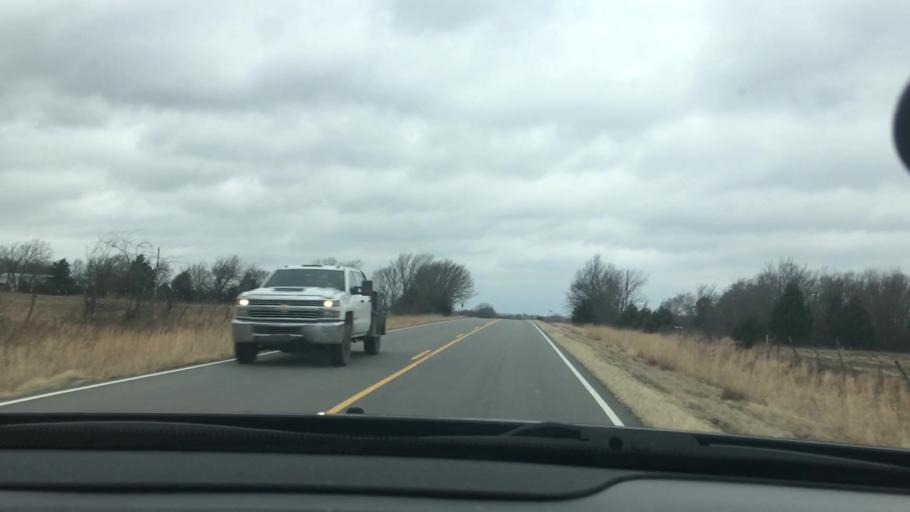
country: US
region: Oklahoma
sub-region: Atoka County
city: Atoka
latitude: 34.3748
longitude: -96.1960
